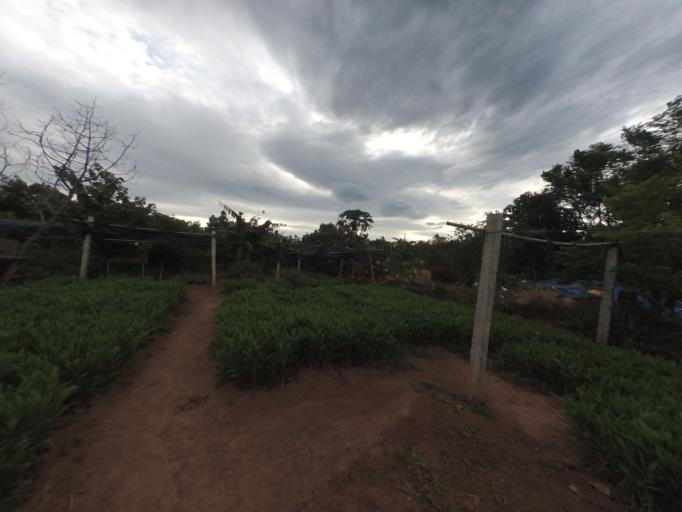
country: VN
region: Quang Tri
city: Cam Lo
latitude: 16.7886
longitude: 107.0019
